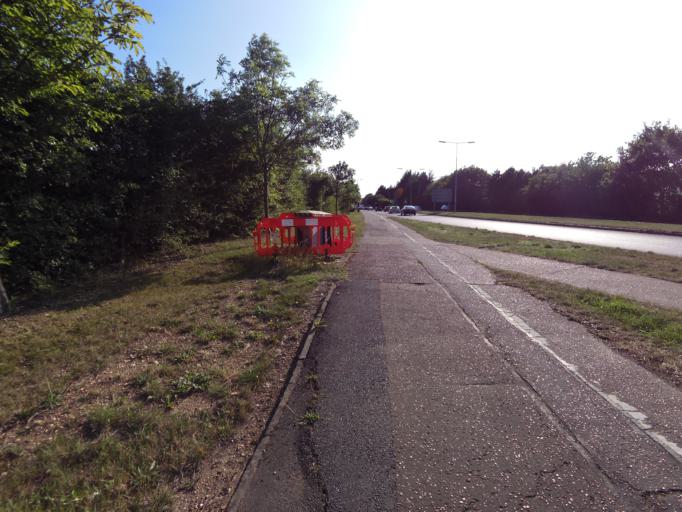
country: GB
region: England
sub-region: Essex
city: Chelmsford
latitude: 51.7533
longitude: 0.5184
